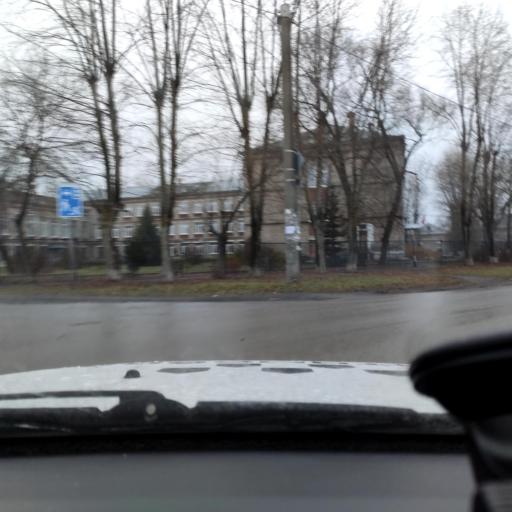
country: RU
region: Perm
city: Perm
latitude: 58.0381
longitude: 56.3520
